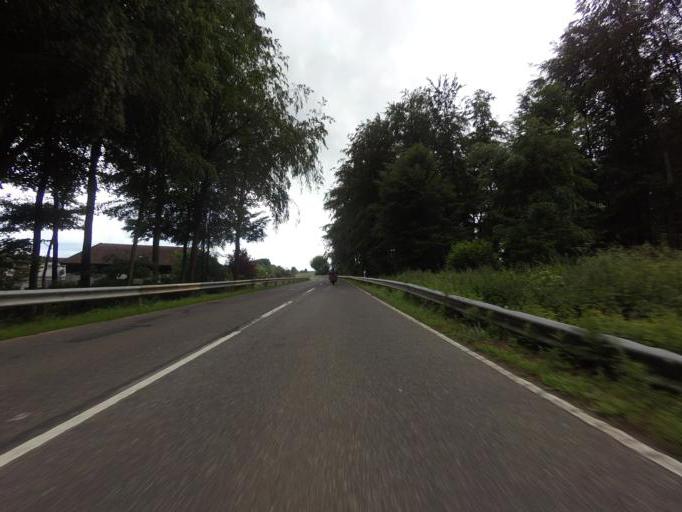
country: DE
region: Rheinland-Pfalz
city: Dungenheim
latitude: 50.2645
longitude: 7.1523
